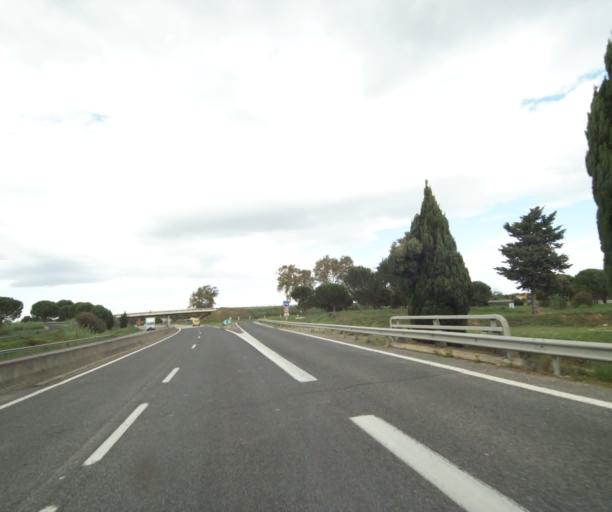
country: FR
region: Languedoc-Roussillon
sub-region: Departement des Pyrenees-Orientales
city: Argelers
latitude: 42.5627
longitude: 3.0059
